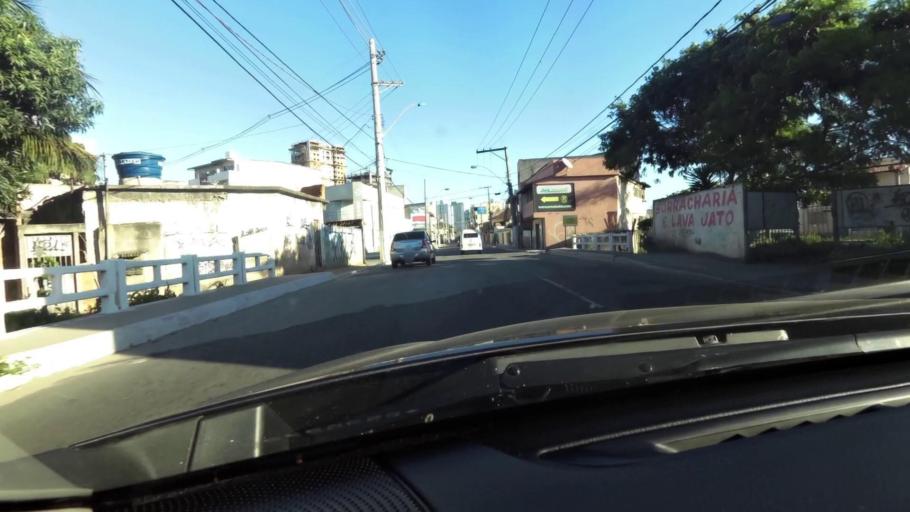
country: BR
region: Espirito Santo
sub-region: Vila Velha
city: Vila Velha
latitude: -20.3546
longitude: -40.2960
